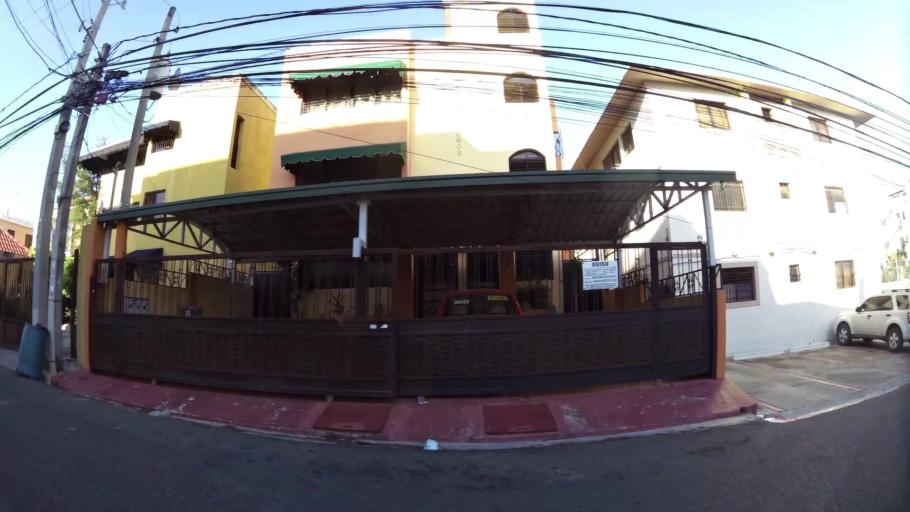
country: DO
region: Nacional
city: Santo Domingo
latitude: 18.4893
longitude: -69.9735
